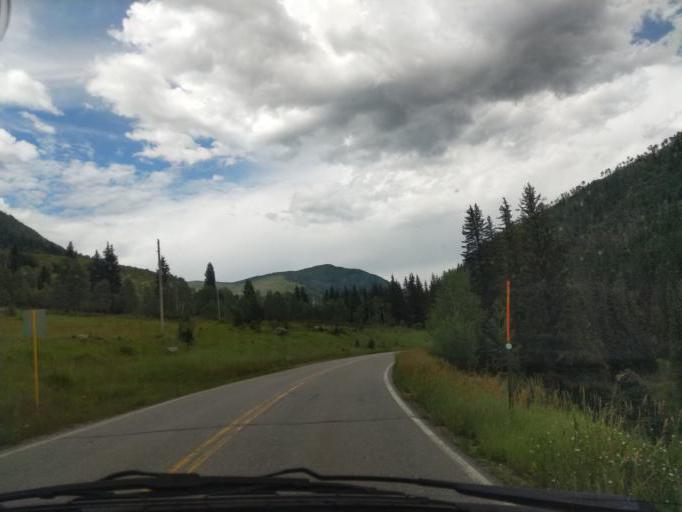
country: US
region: Colorado
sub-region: Garfield County
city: Carbondale
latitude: 39.1025
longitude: -107.2648
